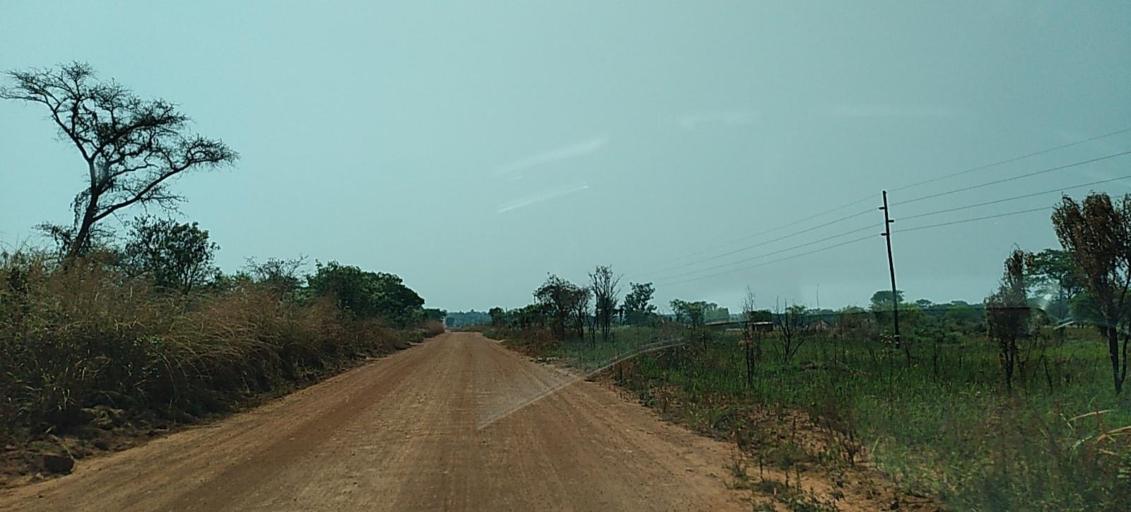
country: ZM
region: North-Western
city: Kansanshi
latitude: -12.0038
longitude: 26.5588
